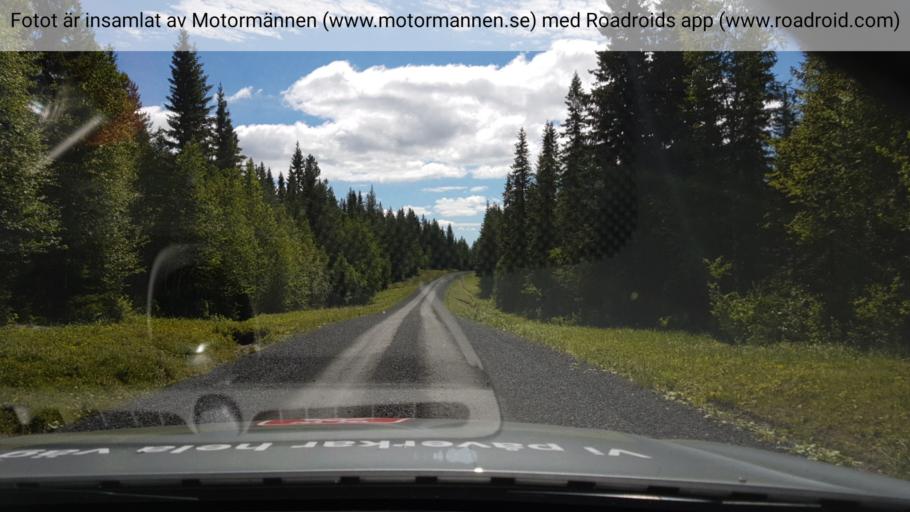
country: SE
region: Jaemtland
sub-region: Krokoms Kommun
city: Valla
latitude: 63.3336
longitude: 13.8391
